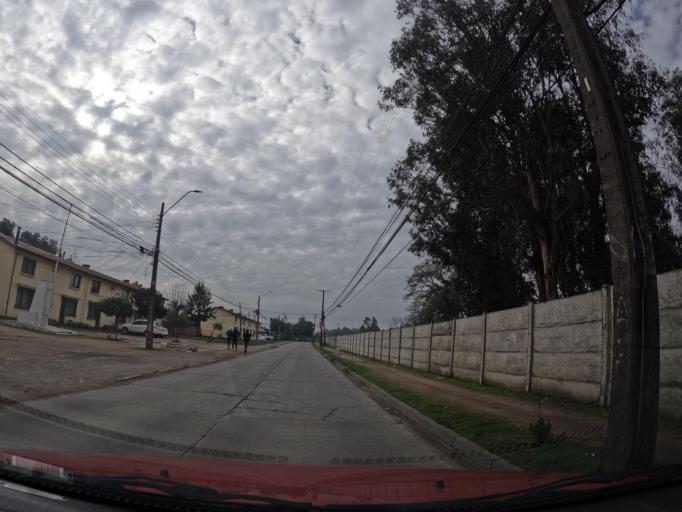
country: CL
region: Maule
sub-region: Provincia de Linares
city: Linares
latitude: -35.8380
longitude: -71.5938
